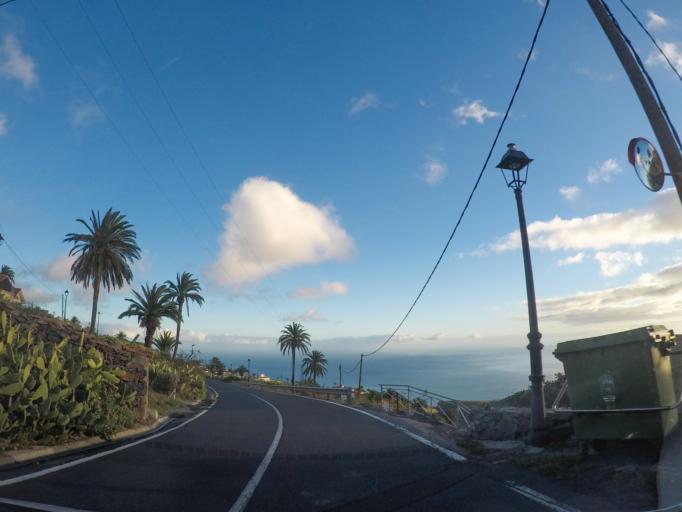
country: ES
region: Canary Islands
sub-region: Provincia de Santa Cruz de Tenerife
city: Alajero
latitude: 28.0618
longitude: -17.2370
